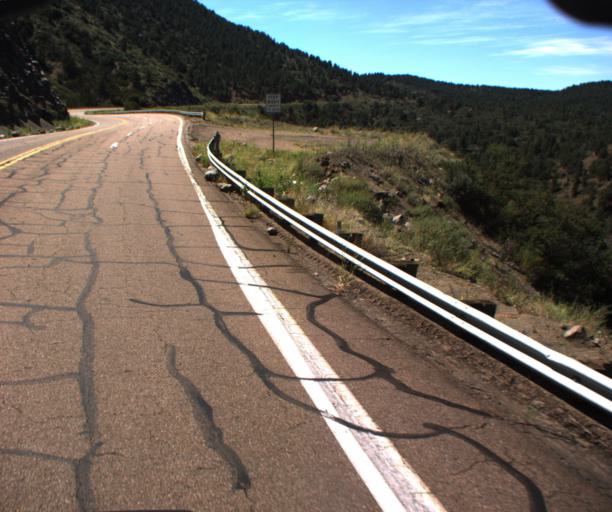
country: US
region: Arizona
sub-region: Navajo County
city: Cibecue
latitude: 33.7858
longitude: -110.5023
